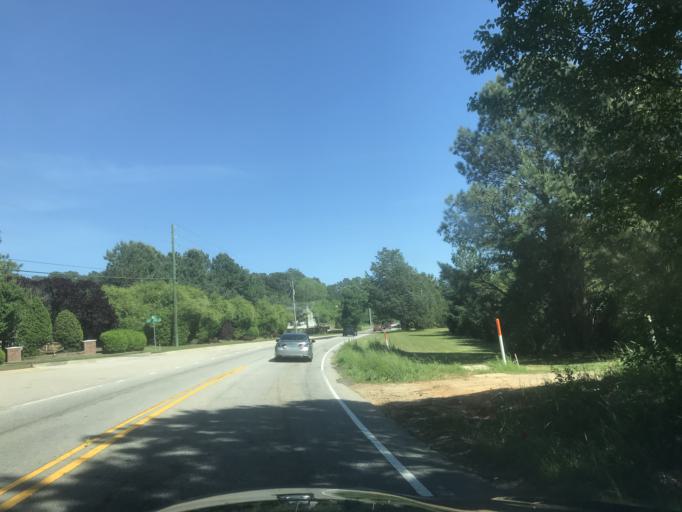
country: US
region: North Carolina
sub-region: Wake County
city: Raleigh
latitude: 35.7419
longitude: -78.6723
